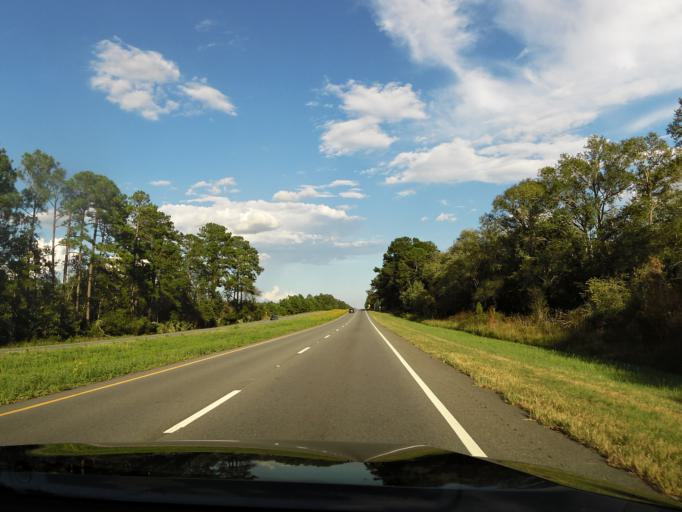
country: US
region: Georgia
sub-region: Brooks County
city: Quitman
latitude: 30.7946
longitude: -83.4368
